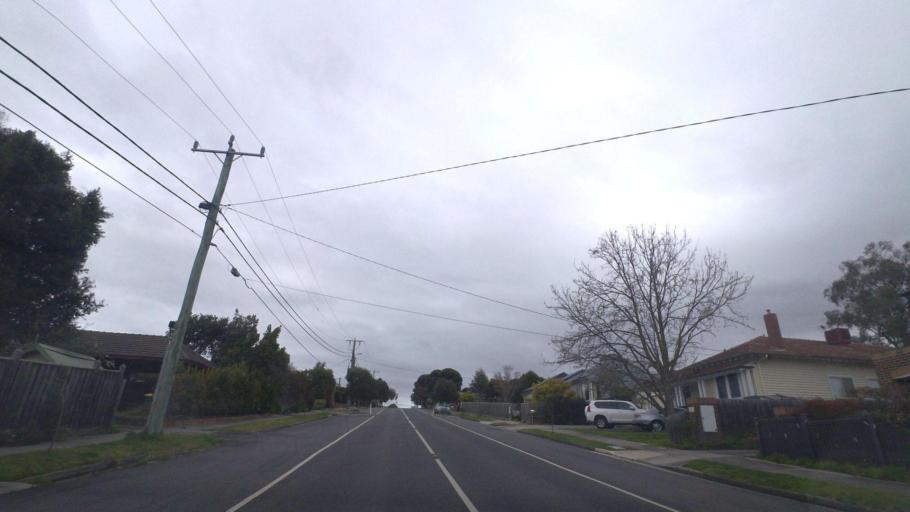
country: AU
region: Victoria
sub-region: Banyule
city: Heidelberg Heights
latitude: -37.7430
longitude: 145.0614
